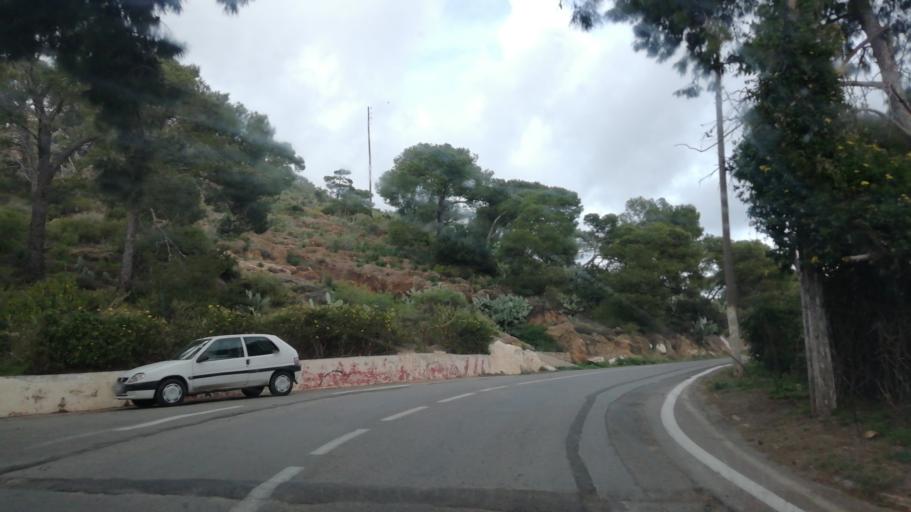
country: DZ
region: Oran
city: Oran
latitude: 35.7027
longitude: -0.6625
